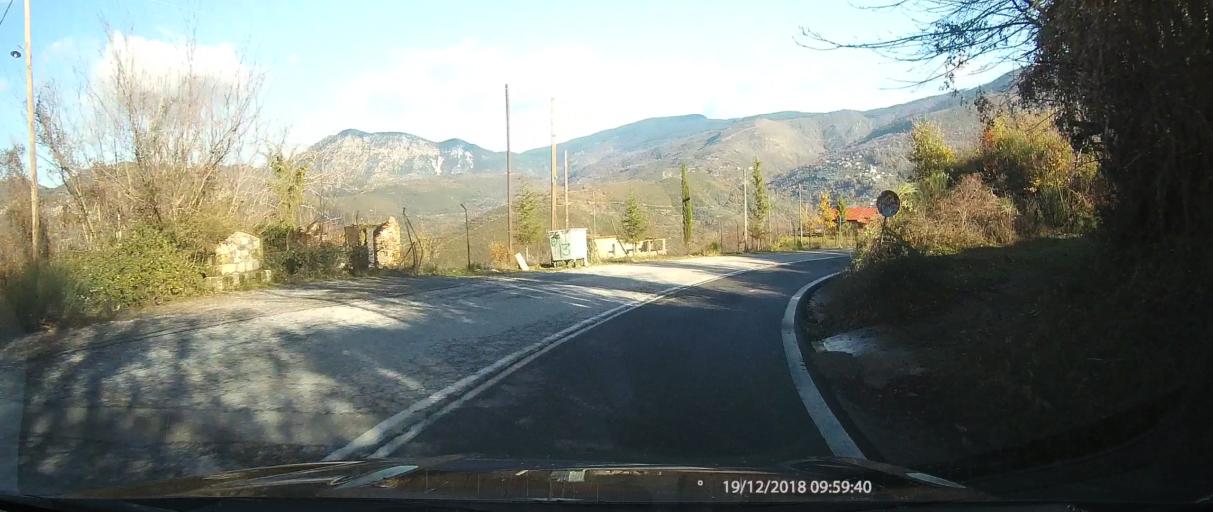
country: GR
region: Peloponnese
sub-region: Nomos Messinias
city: Paralia Vergas
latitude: 37.0951
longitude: 22.2351
